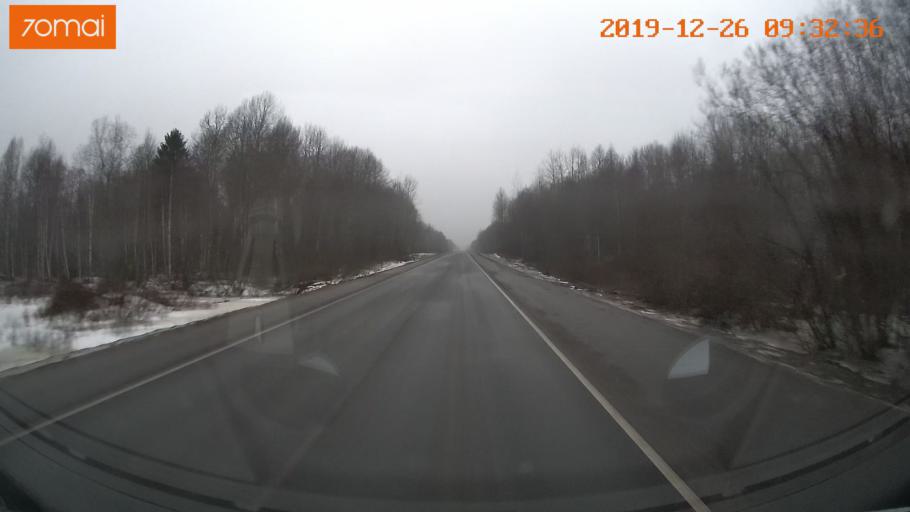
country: RU
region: Vologda
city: Gryazovets
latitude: 59.0798
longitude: 40.1140
